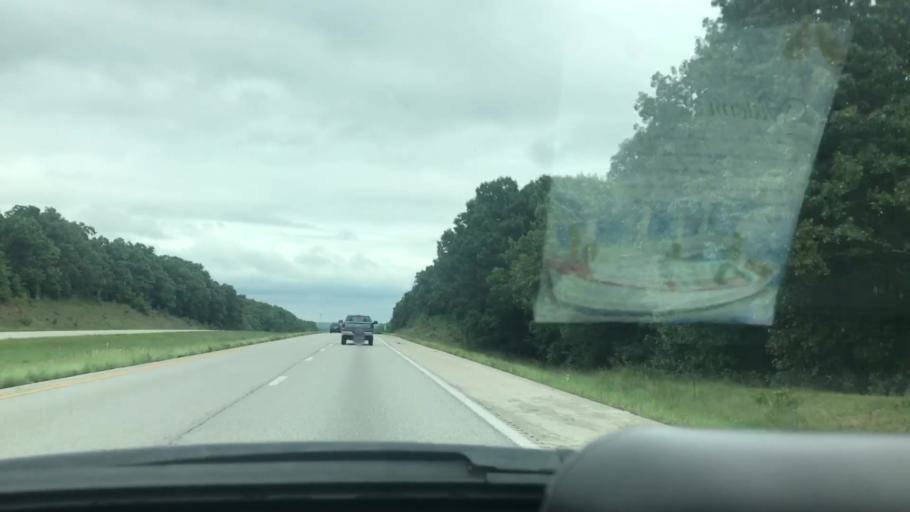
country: US
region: Missouri
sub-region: Lawrence County
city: Mount Vernon
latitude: 37.1448
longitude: -93.7129
